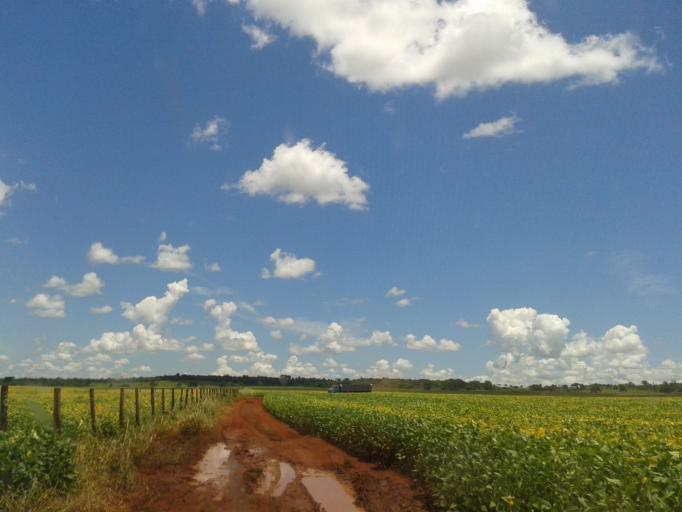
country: BR
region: Minas Gerais
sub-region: Capinopolis
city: Capinopolis
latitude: -18.7698
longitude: -49.7954
